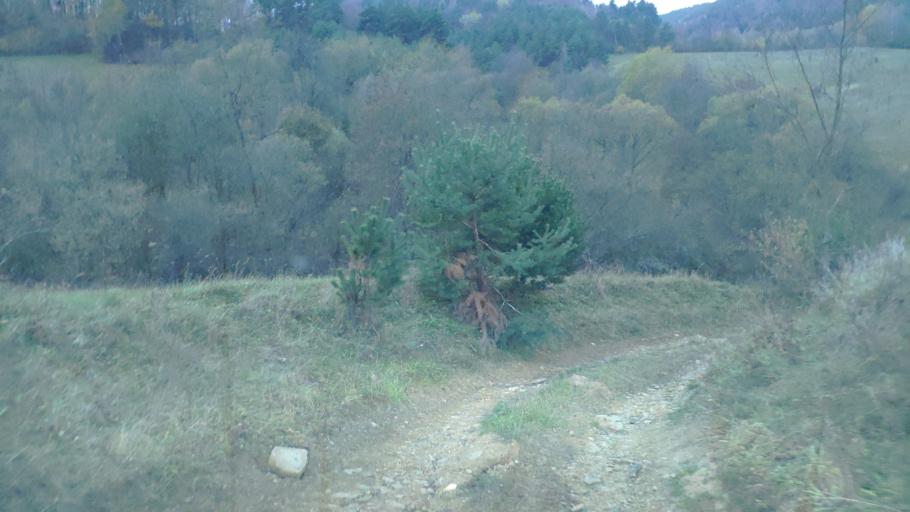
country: SK
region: Presovsky
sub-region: Okres Presov
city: Presov
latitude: 48.9386
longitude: 21.0805
